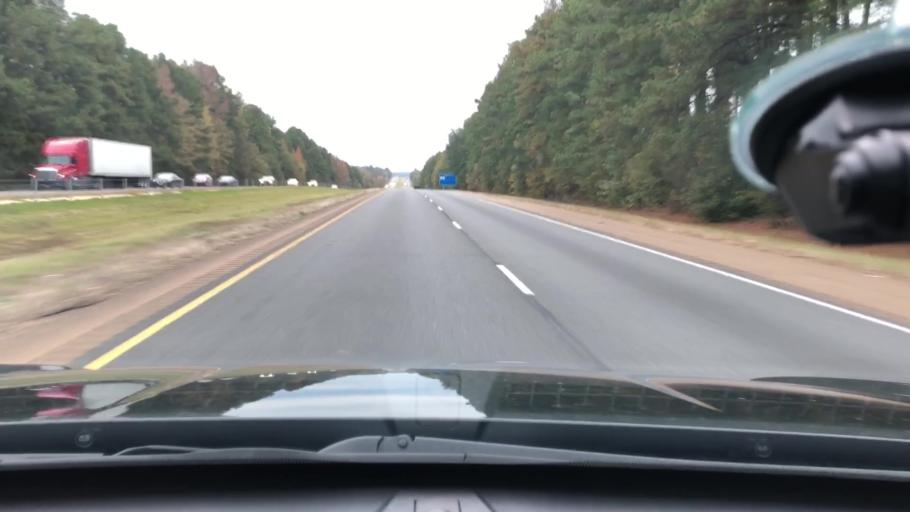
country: US
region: Arkansas
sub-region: Clark County
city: Gurdon
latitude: 33.9760
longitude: -93.2044
